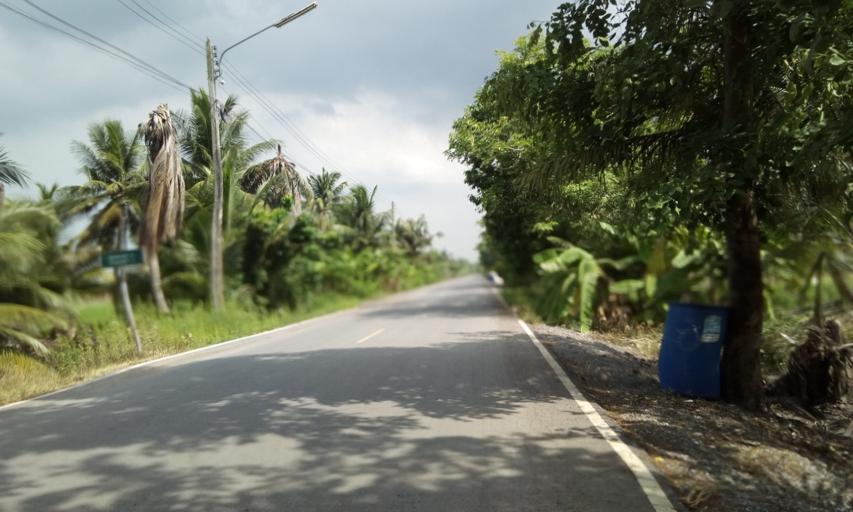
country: TH
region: Pathum Thani
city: Ban Lam Luk Ka
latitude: 14.0282
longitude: 100.8472
